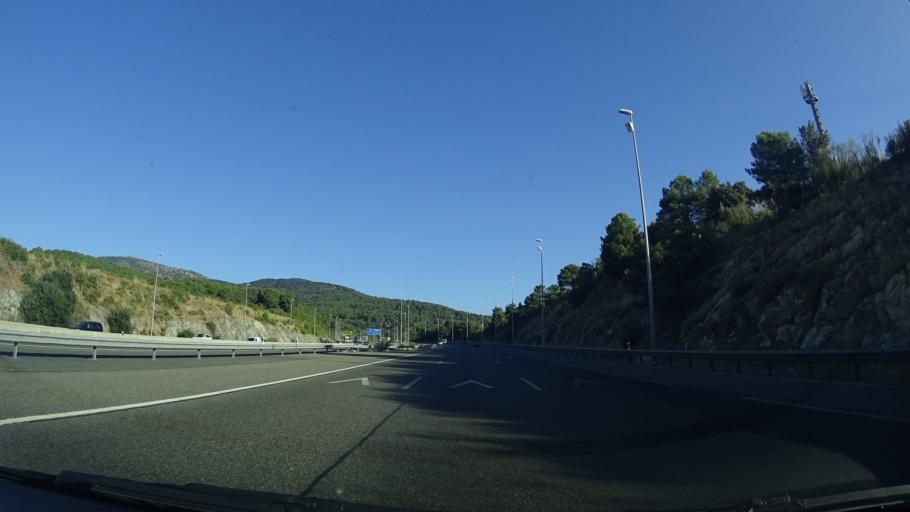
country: ES
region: Madrid
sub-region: Provincia de Madrid
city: Guadarrama
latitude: 40.6738
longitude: -4.1124
